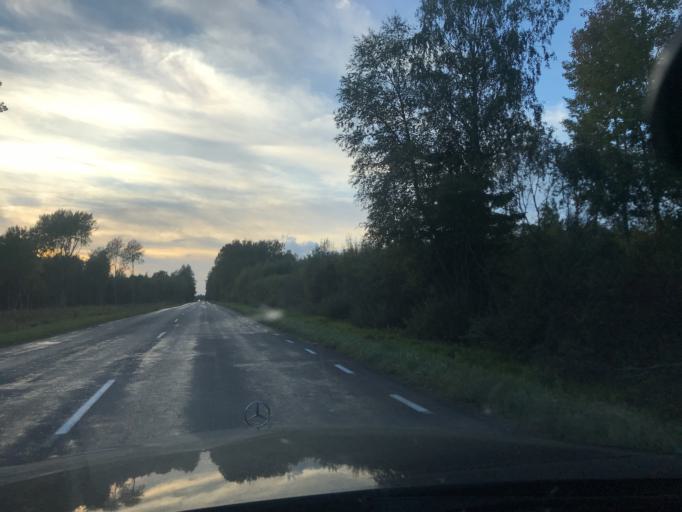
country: EE
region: Vorumaa
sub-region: Antsla vald
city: Vana-Antsla
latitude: 57.9046
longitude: 26.4522
